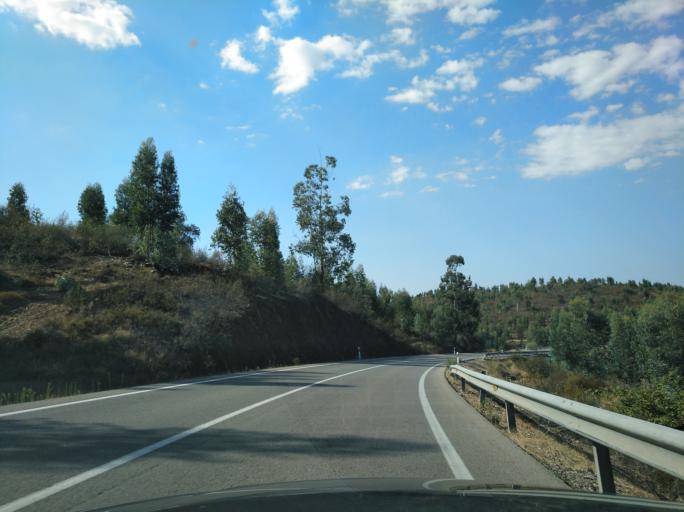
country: ES
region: Andalusia
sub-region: Provincia de Huelva
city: Santa Barbara de Casa
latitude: 37.8147
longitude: -7.2108
